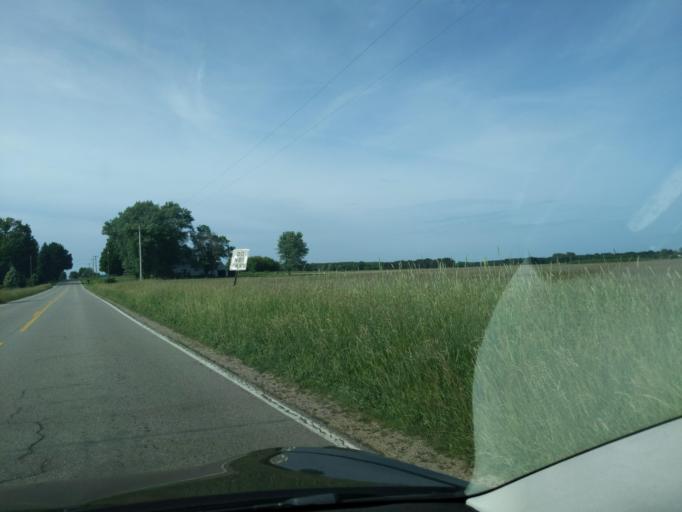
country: US
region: Michigan
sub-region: Newaygo County
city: Fremont
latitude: 43.4215
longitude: -86.0089
